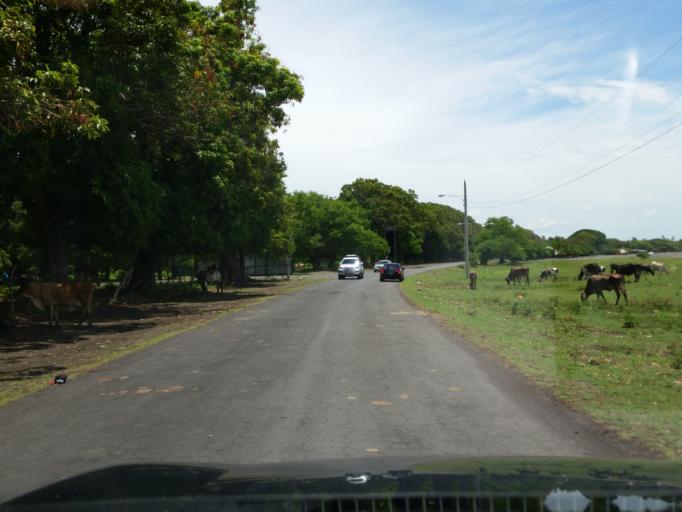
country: NI
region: Granada
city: Granada
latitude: 11.9124
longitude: -85.9308
